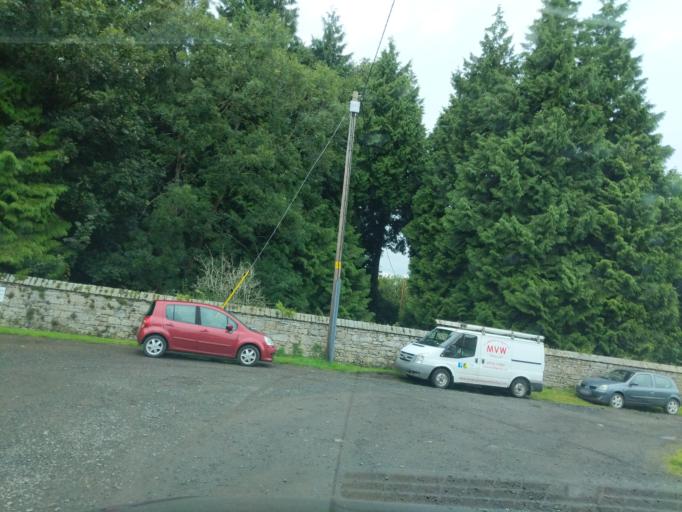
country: GB
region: Scotland
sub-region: Fife
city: Limekilns
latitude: 55.9948
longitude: -3.4753
